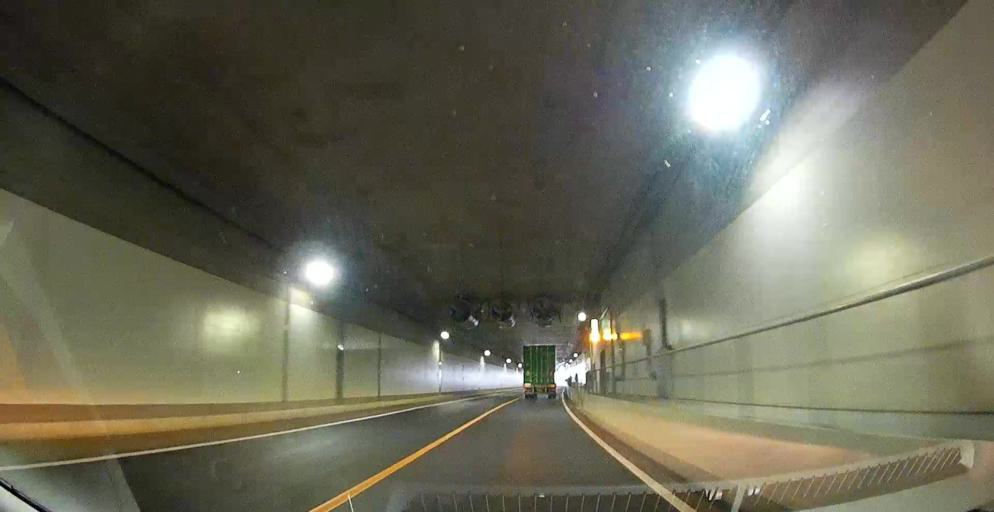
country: JP
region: Tokyo
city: Urayasu
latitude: 35.6153
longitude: 139.7963
